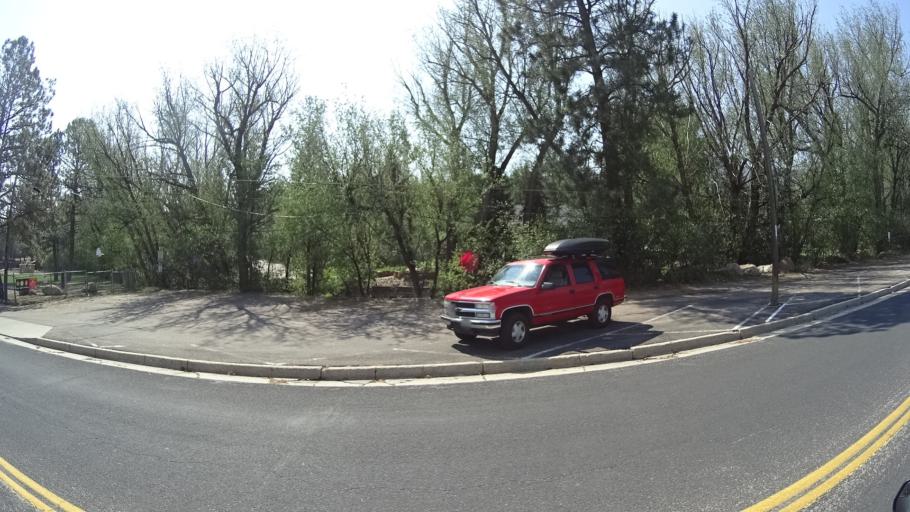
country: US
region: Colorado
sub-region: El Paso County
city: Colorado Springs
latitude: 38.7989
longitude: -104.8502
